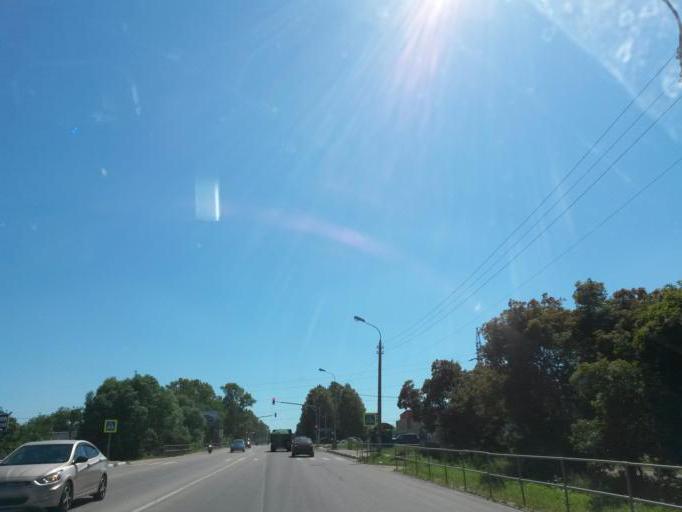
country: RU
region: Moskovskaya
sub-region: Chekhovskiy Rayon
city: Chekhov
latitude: 55.1298
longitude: 37.4515
